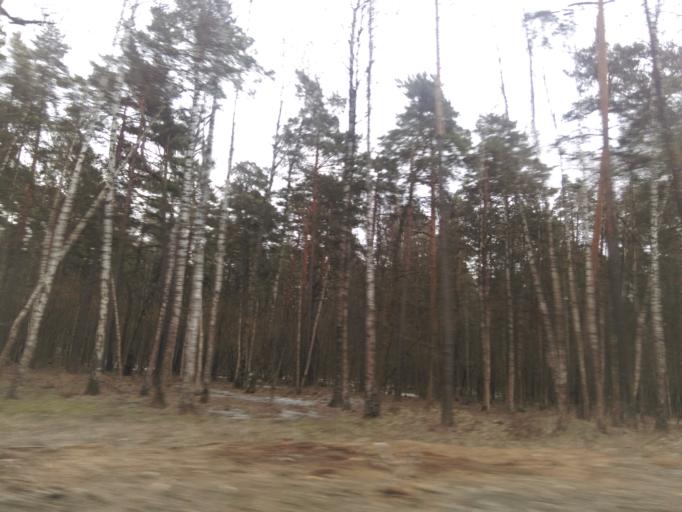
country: RU
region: Moscow
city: Rublevo
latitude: 55.7528
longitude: 37.3358
